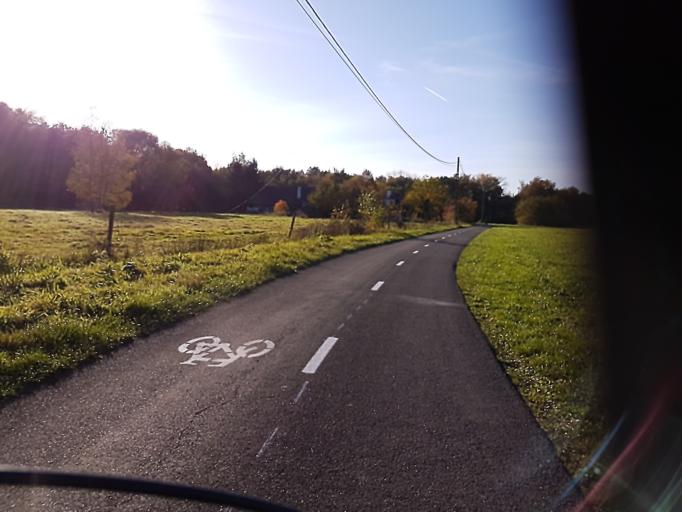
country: BE
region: Flanders
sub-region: Provincie Antwerpen
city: Bonheiden
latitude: 51.0415
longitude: 4.5471
